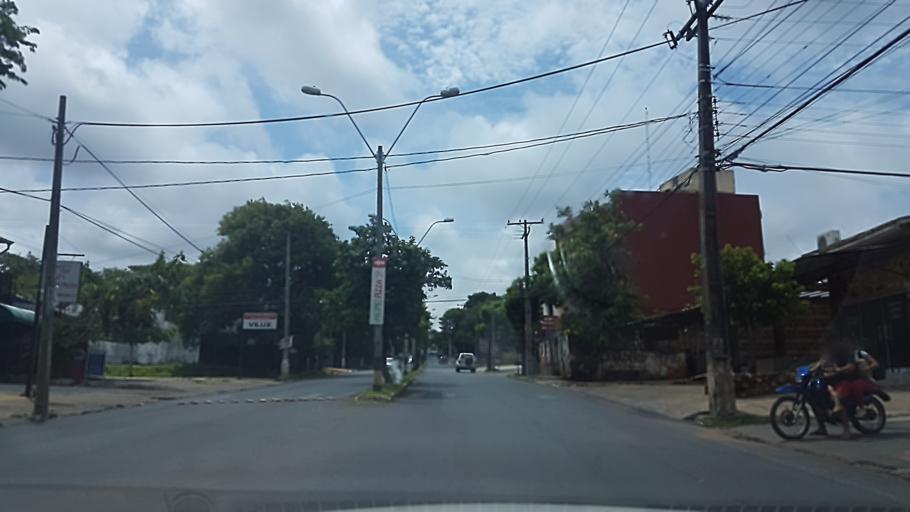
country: PY
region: Central
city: Villa Elisa
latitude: -25.3615
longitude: -57.5930
